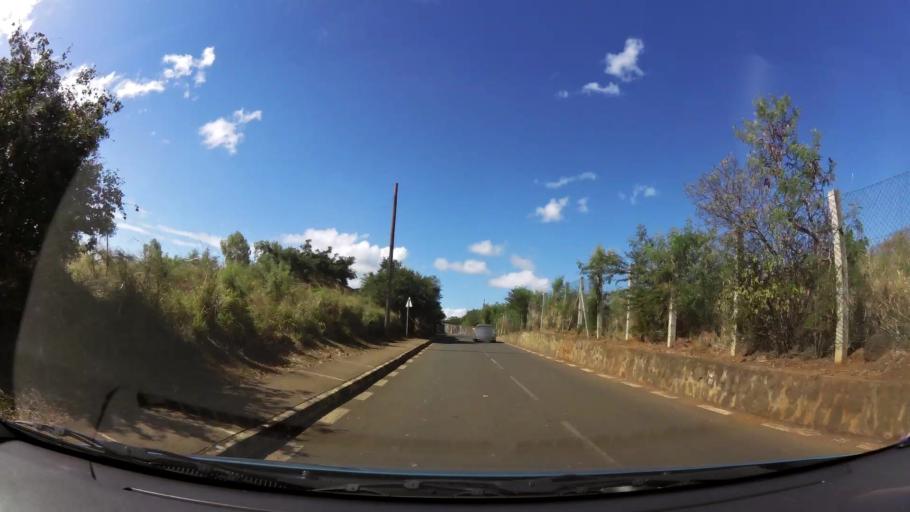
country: MU
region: Black River
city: Gros Cailloux
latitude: -20.2309
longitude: 57.4270
